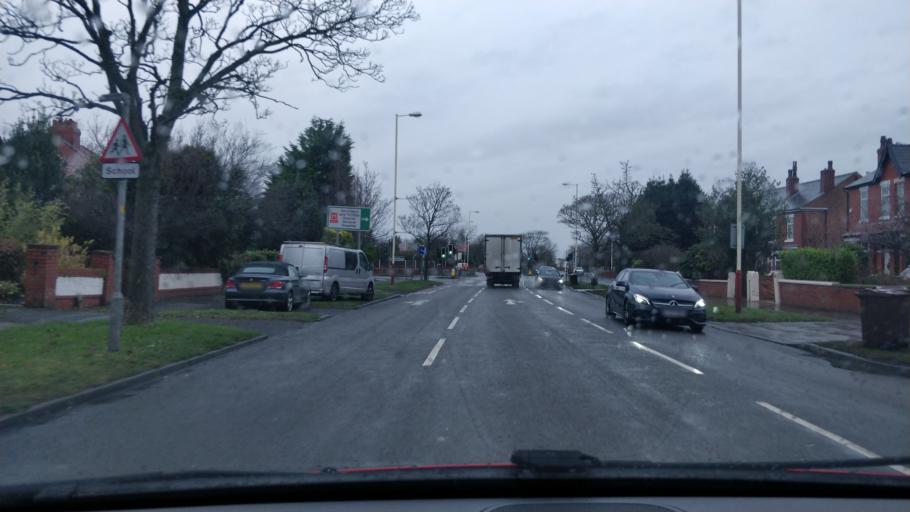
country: GB
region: England
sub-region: Sefton
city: Southport
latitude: 53.6119
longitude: -3.0215
